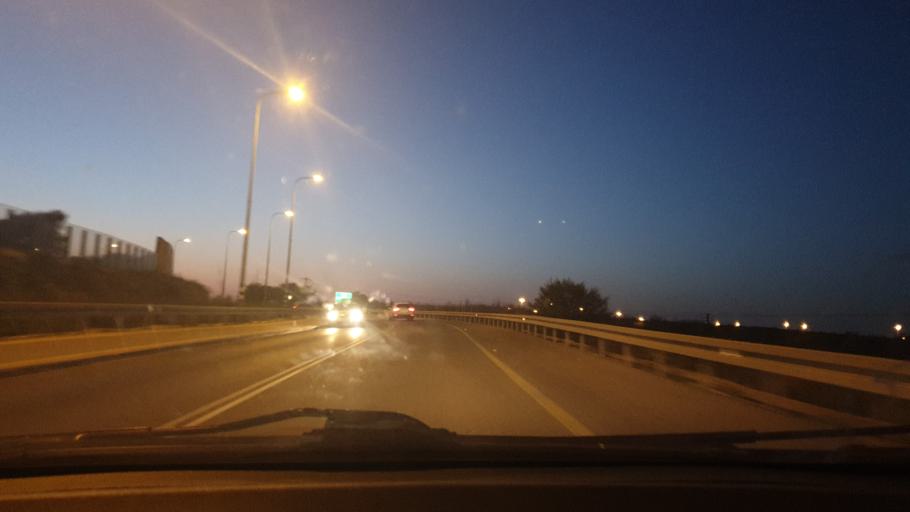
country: IL
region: Central District
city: Bene 'Ayish
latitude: 31.7937
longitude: 34.7649
